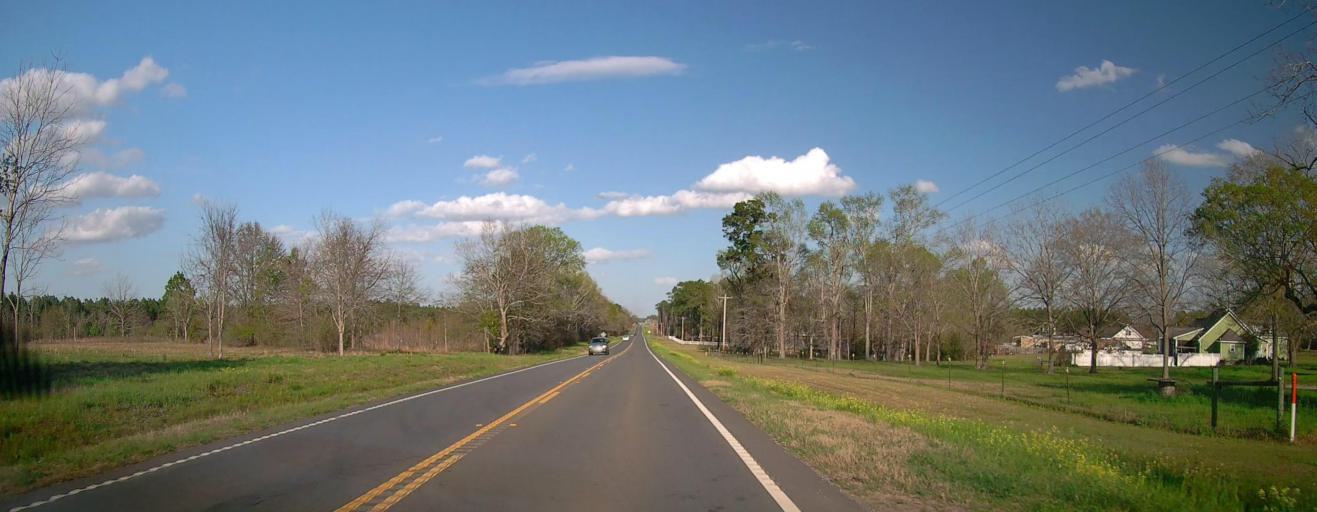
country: US
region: Georgia
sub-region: Toombs County
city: Vidalia
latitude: 32.2027
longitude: -82.4885
